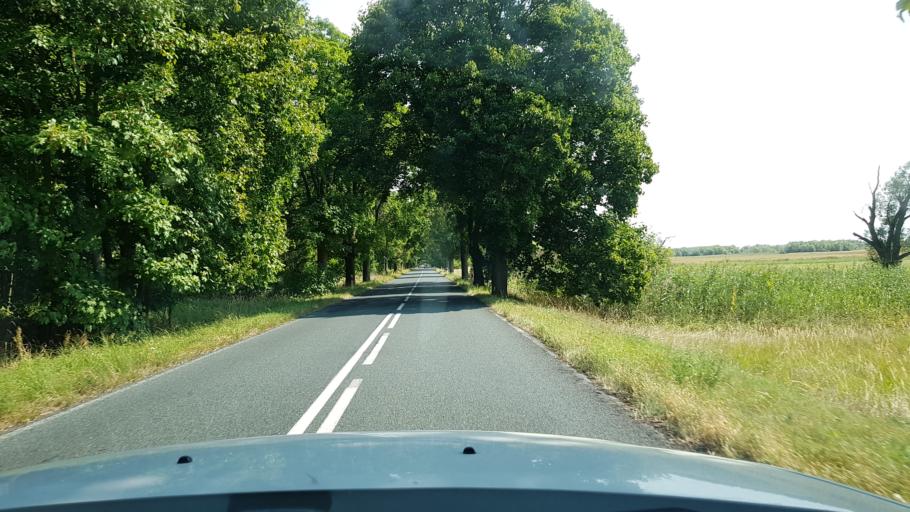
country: PL
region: West Pomeranian Voivodeship
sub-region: Powiat gryfinski
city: Cedynia
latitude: 52.8313
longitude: 14.2124
